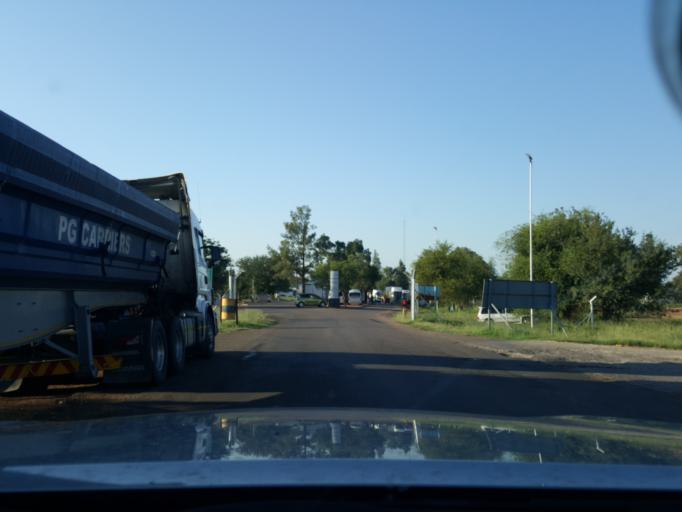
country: ZA
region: North-West
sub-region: Ngaka Modiri Molema District Municipality
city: Mmabatho
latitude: -25.6372
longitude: 25.5740
